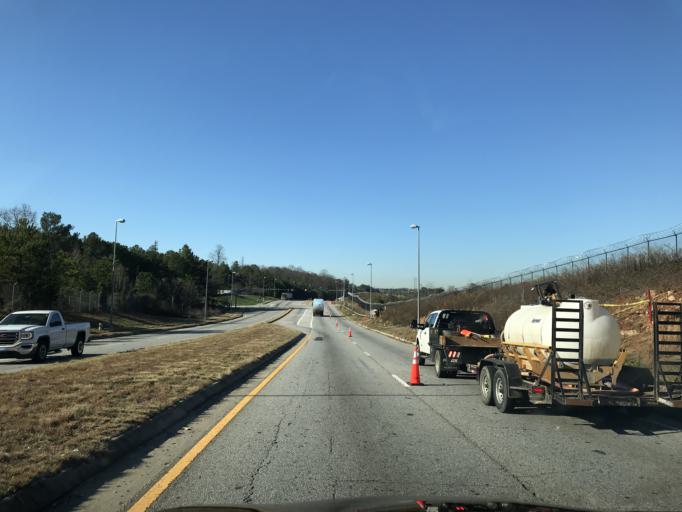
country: US
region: Georgia
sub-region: Fulton County
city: Hapeville
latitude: 33.6186
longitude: -84.4232
